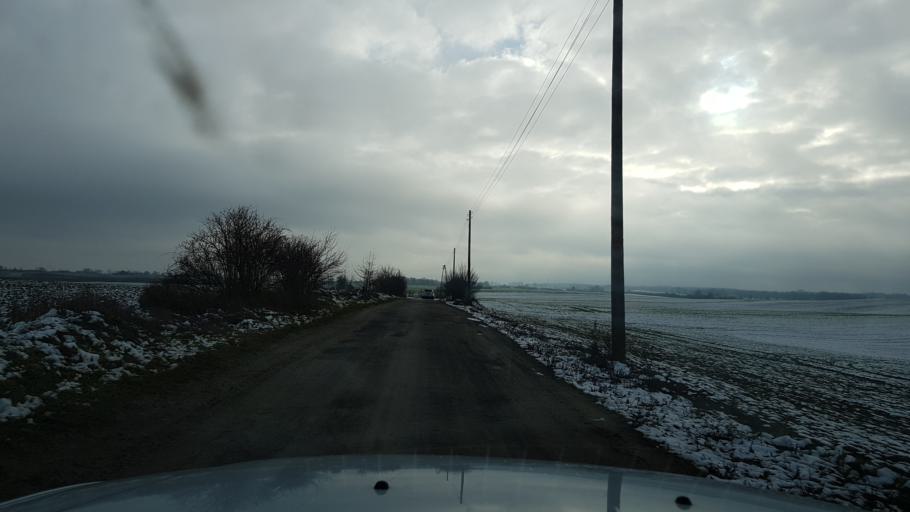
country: PL
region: West Pomeranian Voivodeship
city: Trzcinsko Zdroj
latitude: 52.9606
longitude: 14.6770
